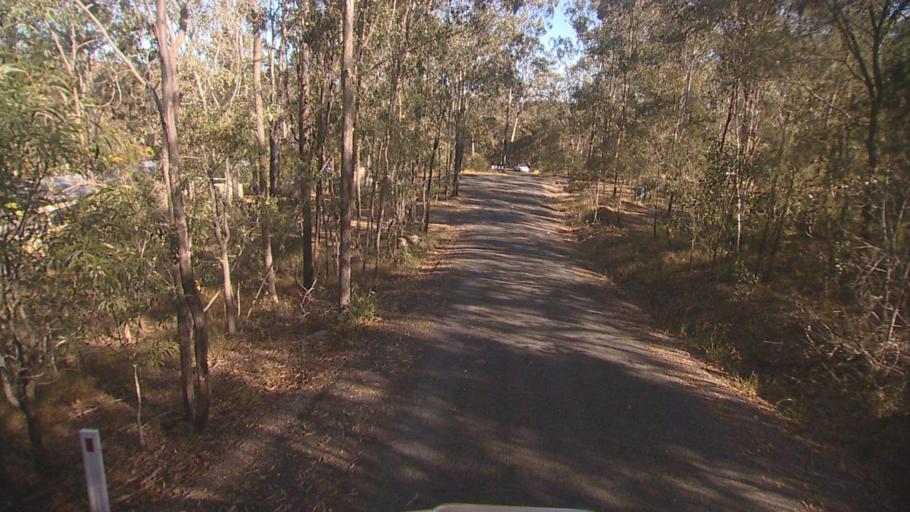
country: AU
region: Queensland
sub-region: Ipswich
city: Springfield Lakes
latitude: -27.6902
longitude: 152.9319
